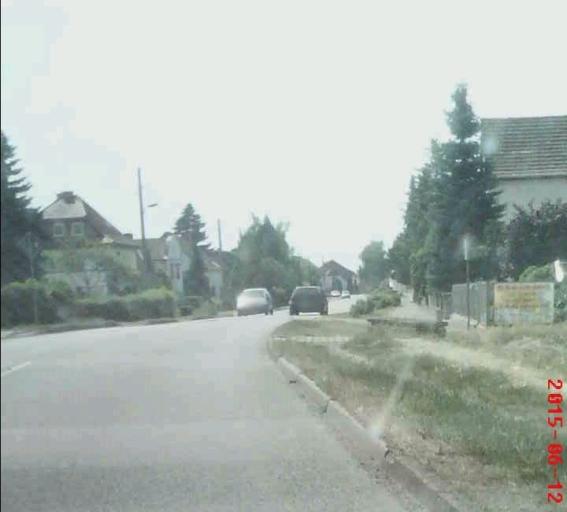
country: DE
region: Saxony-Anhalt
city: Rossla
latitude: 51.4642
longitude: 11.0823
